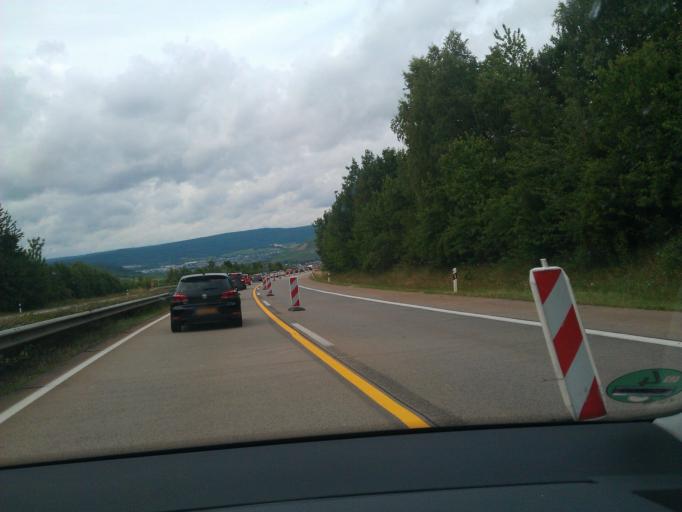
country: DE
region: Rheinland-Pfalz
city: Longuich
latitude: 49.7869
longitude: 6.7809
